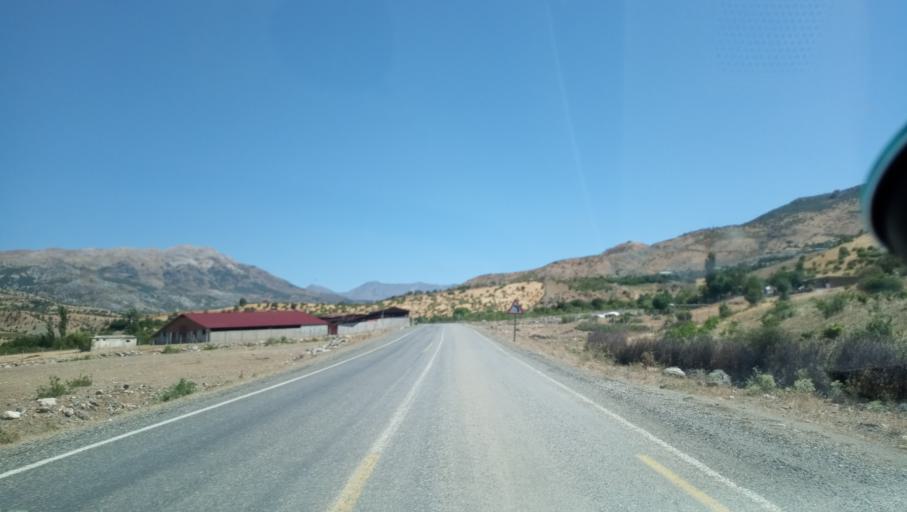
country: TR
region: Diyarbakir
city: Kulp
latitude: 38.4963
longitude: 41.0454
